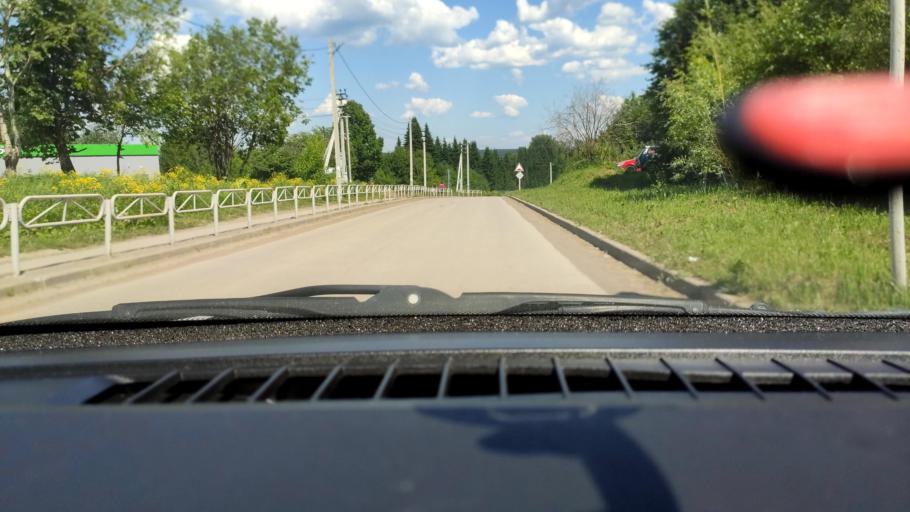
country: RU
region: Perm
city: Sylva
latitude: 58.0328
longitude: 56.7514
